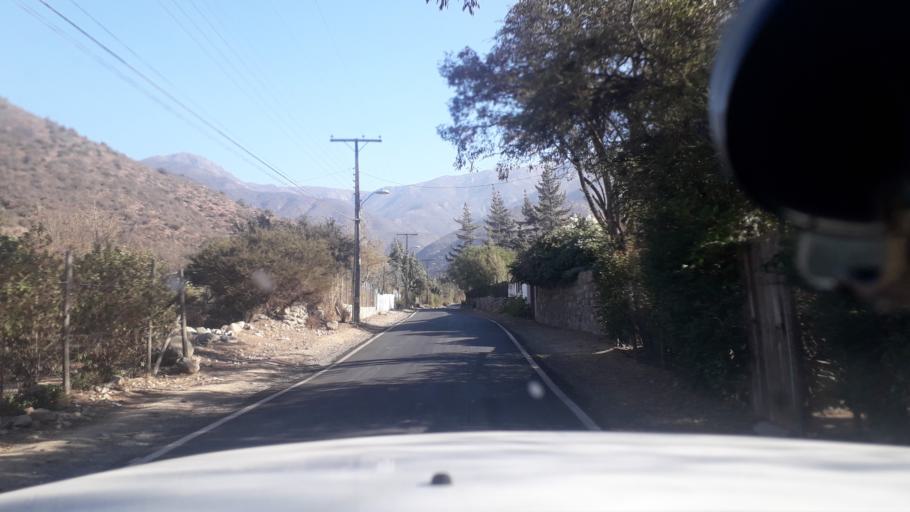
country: CL
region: Valparaiso
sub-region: Provincia de Marga Marga
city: Limache
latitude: -33.0558
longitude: -71.1129
